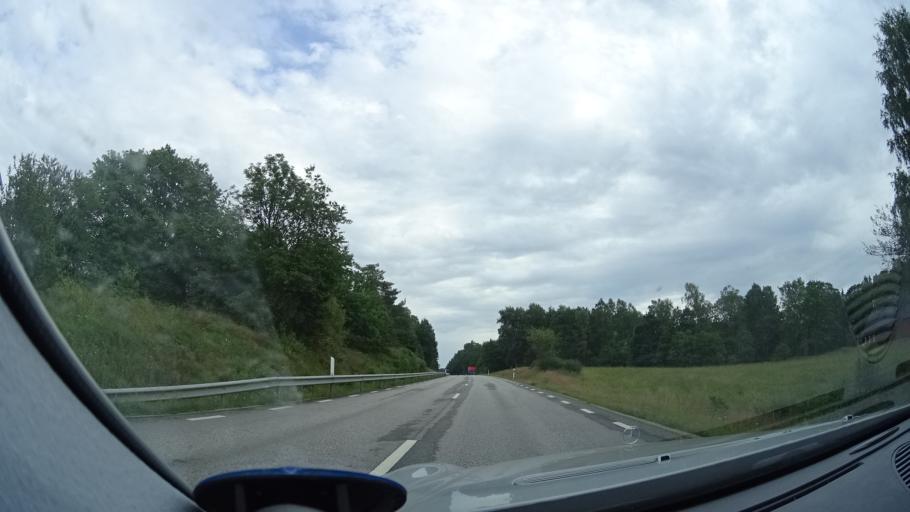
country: SE
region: Kronoberg
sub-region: Tingsryds Kommun
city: Tingsryd
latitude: 56.4736
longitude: 15.0068
